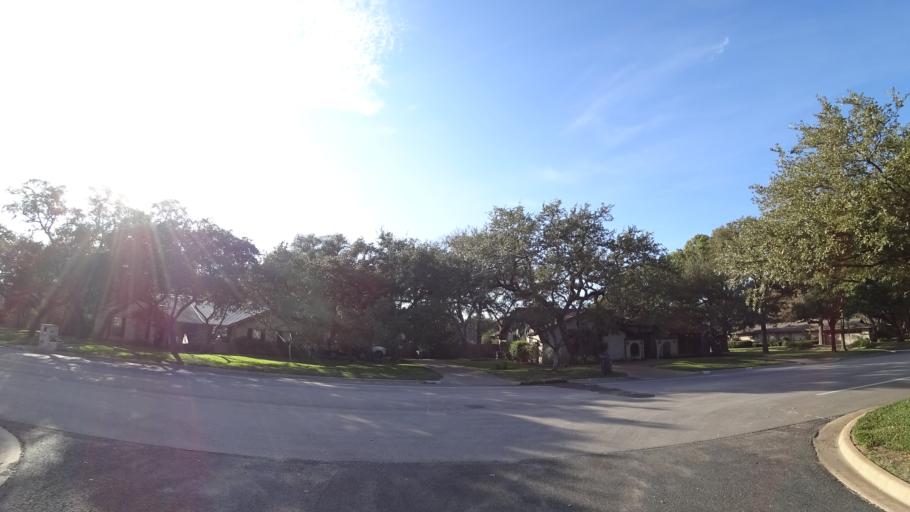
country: US
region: Texas
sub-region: Williamson County
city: Anderson Mill
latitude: 30.4331
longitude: -97.8060
